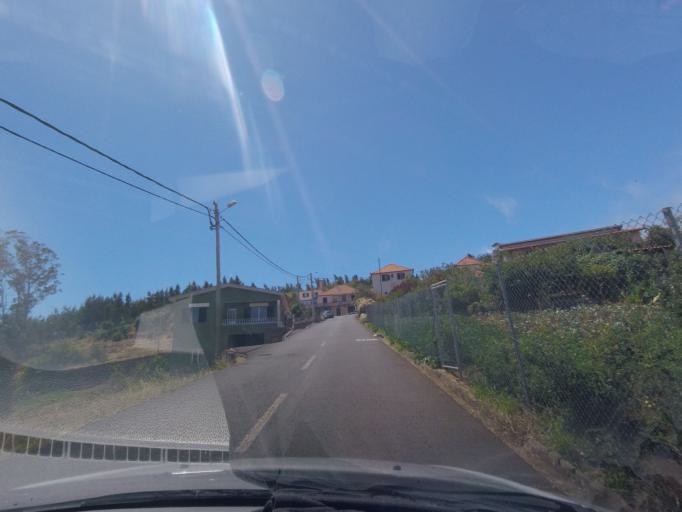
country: PT
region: Madeira
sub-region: Santa Cruz
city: Camacha
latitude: 32.6941
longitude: -16.8362
